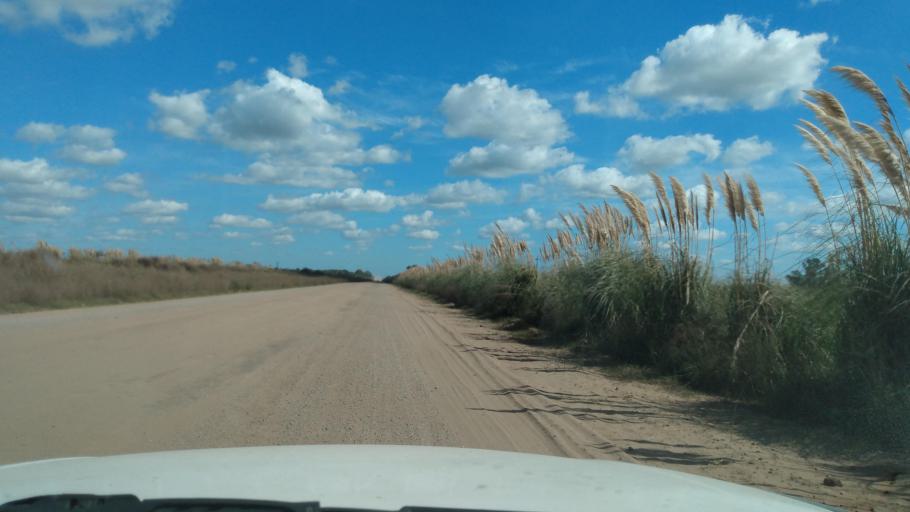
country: AR
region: Buenos Aires
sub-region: Partido de Navarro
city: Navarro
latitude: -35.0040
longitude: -59.3683
